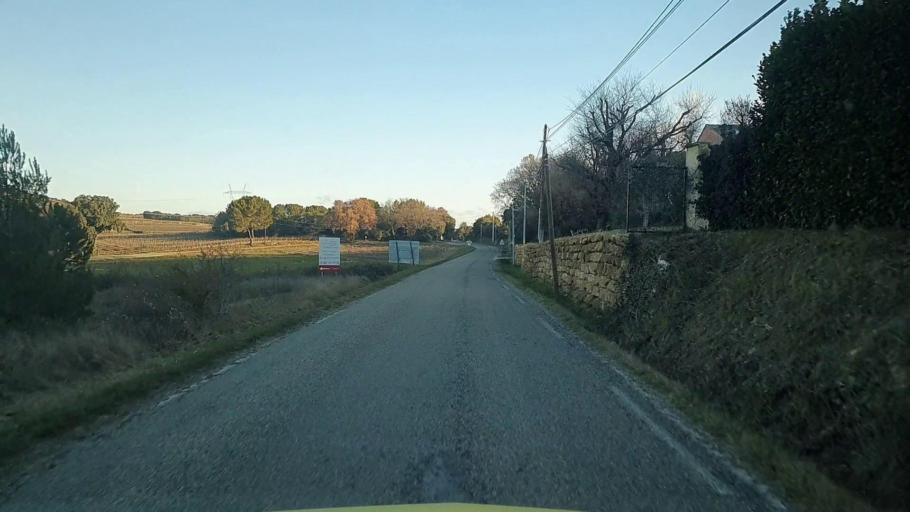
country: FR
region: Languedoc-Roussillon
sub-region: Departement du Gard
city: Venejan
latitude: 44.2035
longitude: 4.6605
